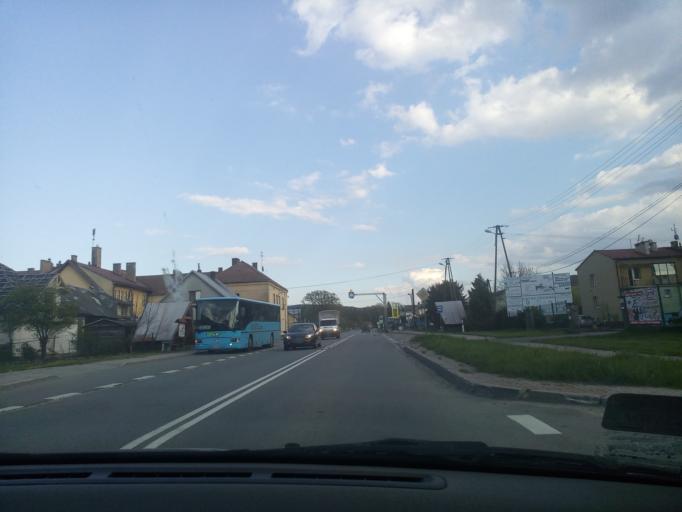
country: PL
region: Lesser Poland Voivodeship
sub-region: Powiat nowosadecki
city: Labowa
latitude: 49.5284
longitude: 20.8544
